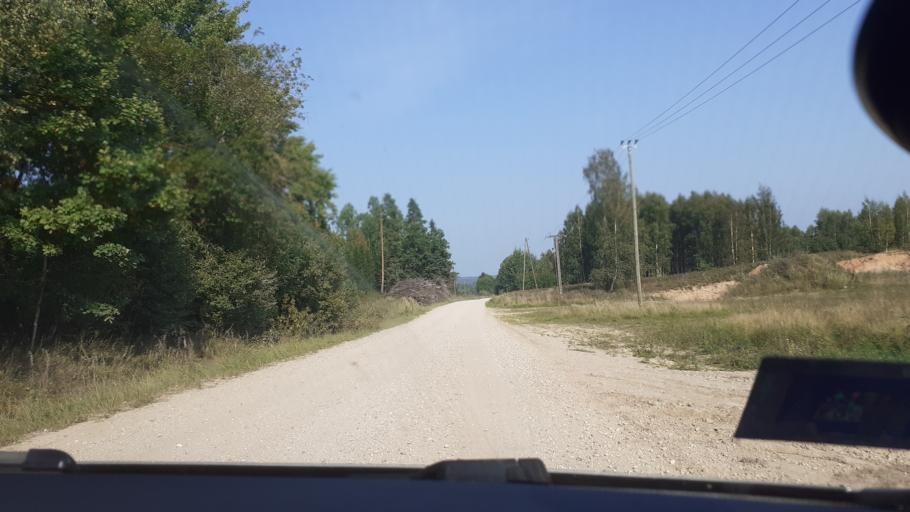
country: LV
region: Kuldigas Rajons
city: Kuldiga
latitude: 56.9807
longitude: 21.8579
